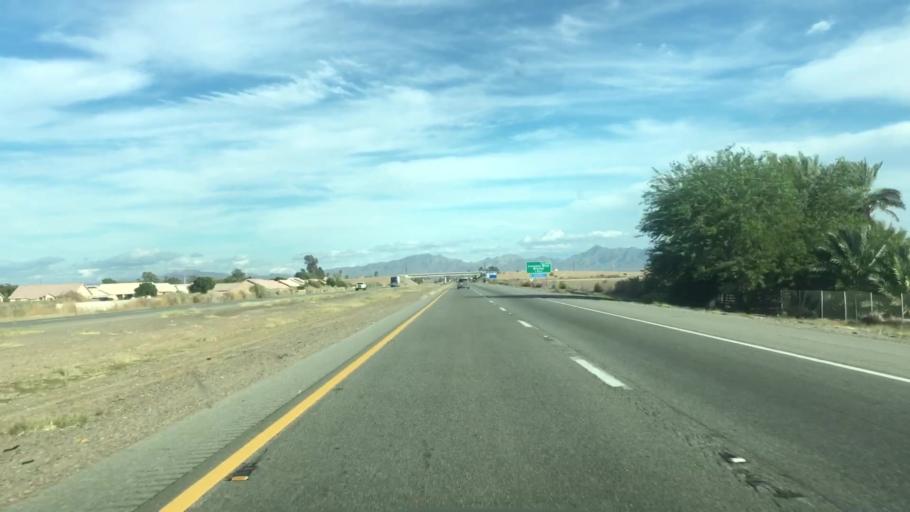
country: US
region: California
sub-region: Riverside County
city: Blythe
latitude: 33.6070
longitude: -114.6316
